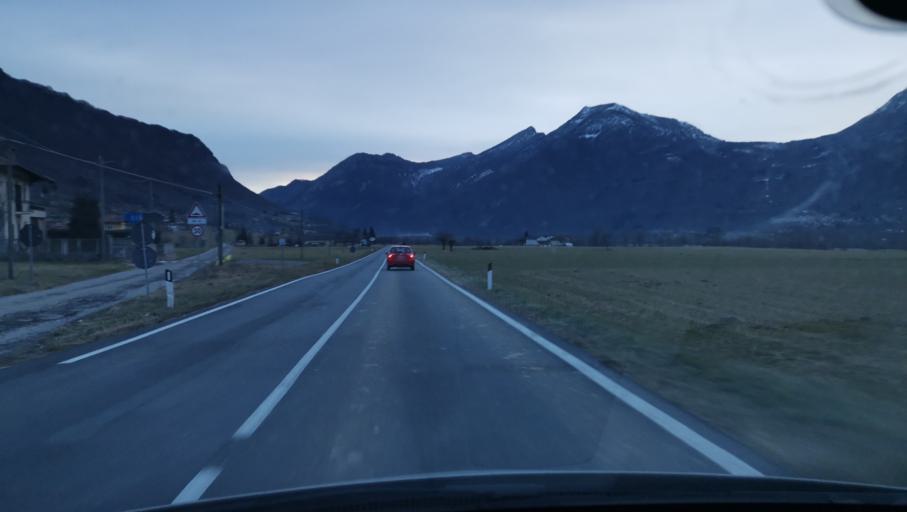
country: IT
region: Piedmont
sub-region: Provincia di Cuneo
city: Demonte
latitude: 44.3152
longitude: 7.3225
